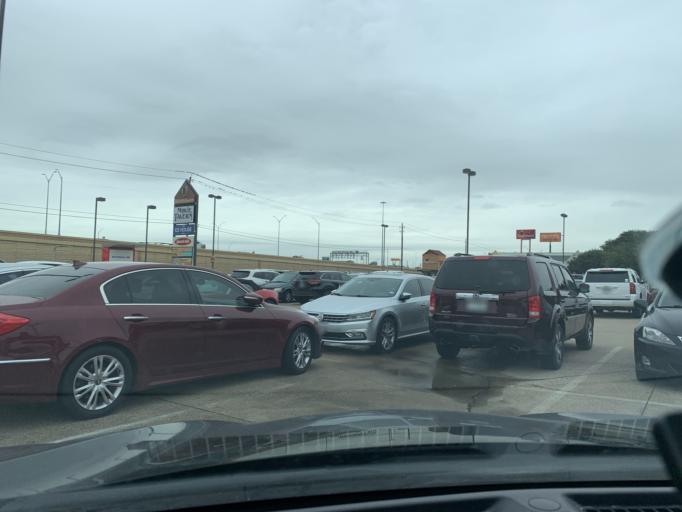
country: US
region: Texas
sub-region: Tarrant County
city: Bedford
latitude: 32.8357
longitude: -97.1321
